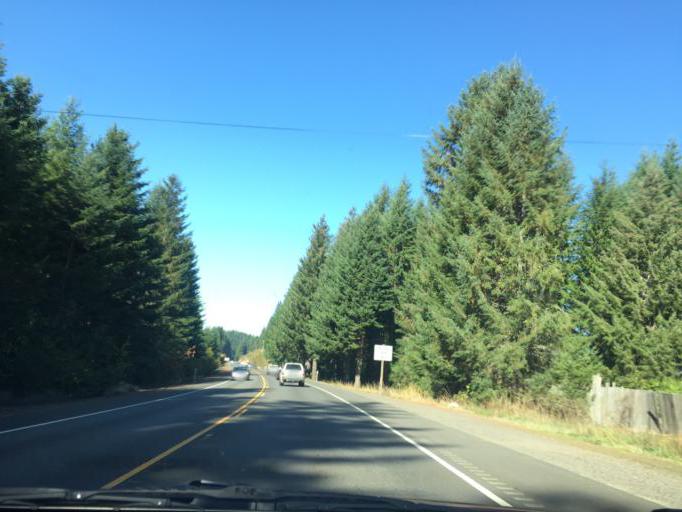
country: US
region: Oregon
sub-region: Columbia County
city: Vernonia
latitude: 45.7357
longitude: -123.2583
